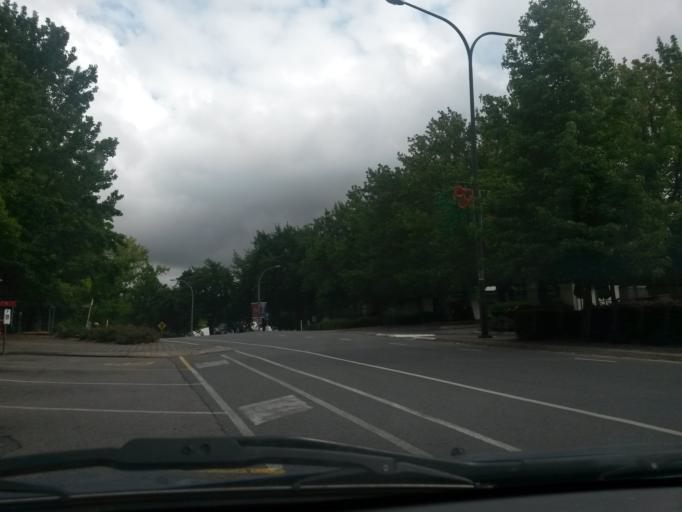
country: AU
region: South Australia
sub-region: Adelaide Hills
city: Heathfield
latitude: -35.0041
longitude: 138.7164
